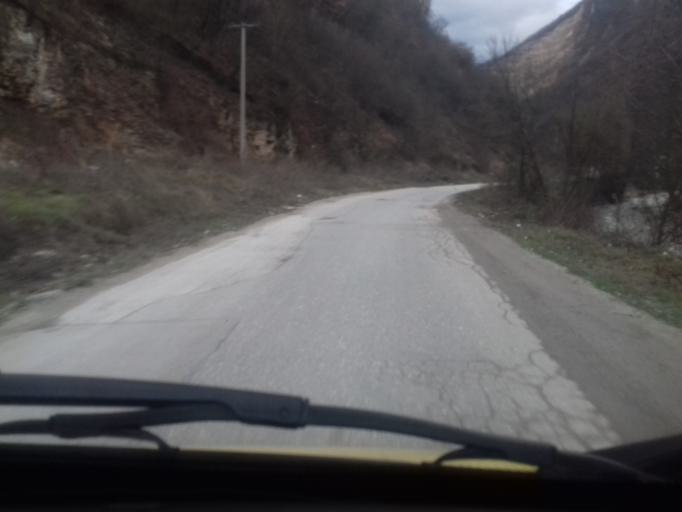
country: BA
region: Federation of Bosnia and Herzegovina
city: Zenica
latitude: 44.2144
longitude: 17.9398
